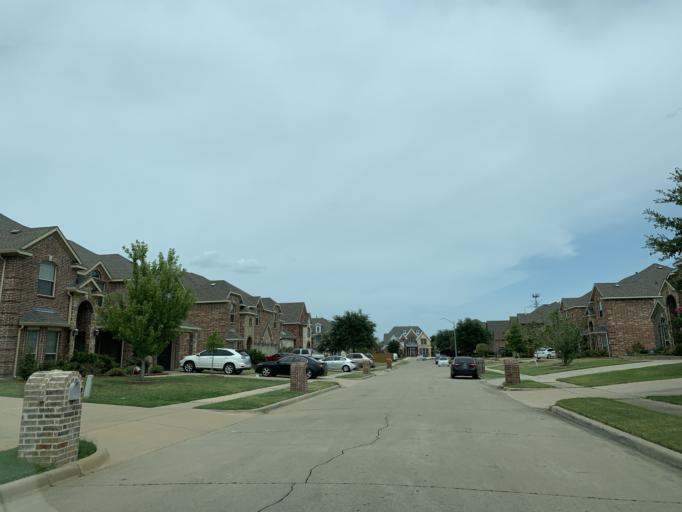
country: US
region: Texas
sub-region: Dallas County
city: Grand Prairie
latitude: 32.6555
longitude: -97.0381
